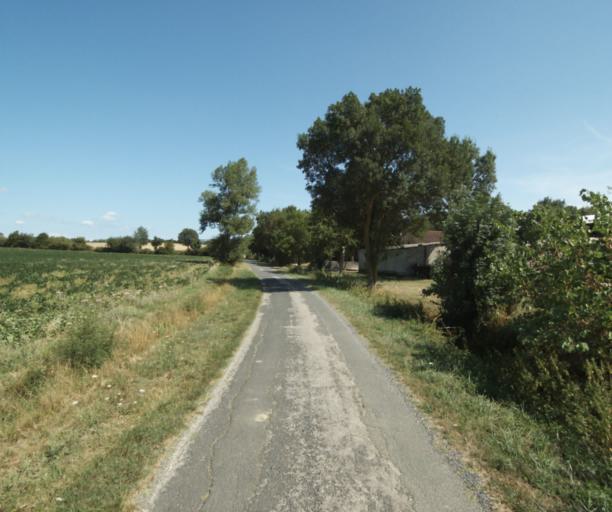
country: FR
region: Midi-Pyrenees
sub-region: Departement de la Haute-Garonne
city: Revel
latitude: 43.4880
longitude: 1.9941
